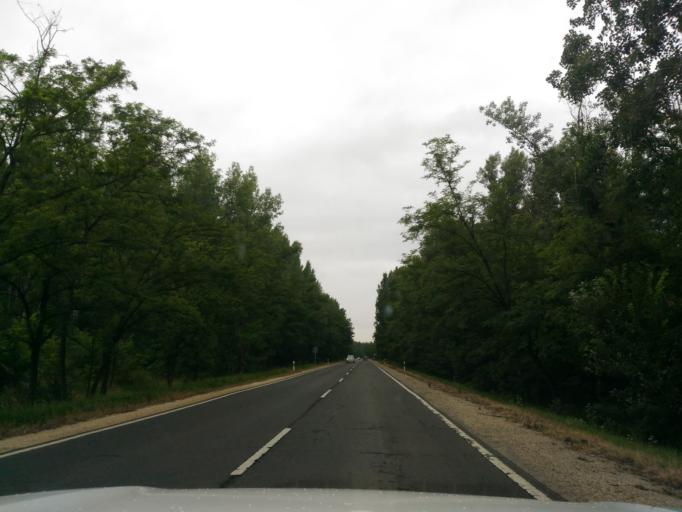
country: HU
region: Pest
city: Alsonemedi
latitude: 47.2912
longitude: 19.1886
